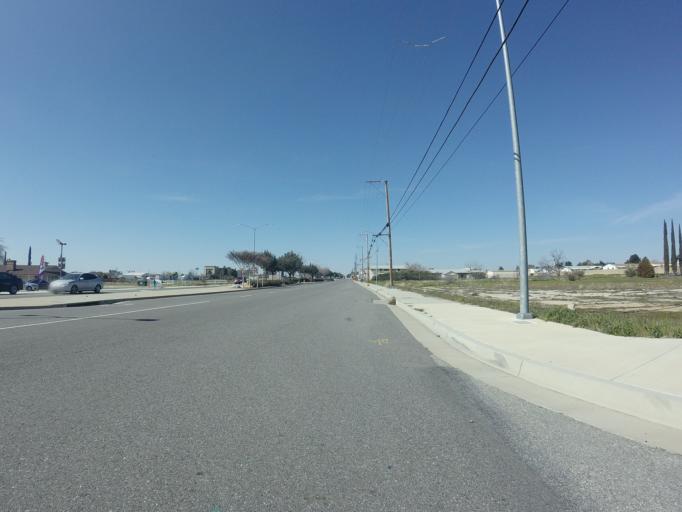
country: US
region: California
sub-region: Riverside County
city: Beaumont
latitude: 33.9293
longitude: -116.9383
